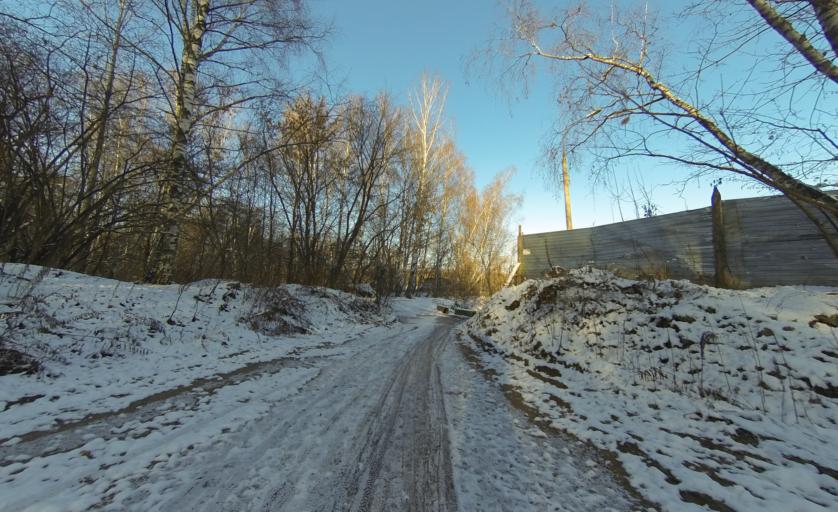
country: RU
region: Moscow
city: Rostokino
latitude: 55.8314
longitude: 37.6935
